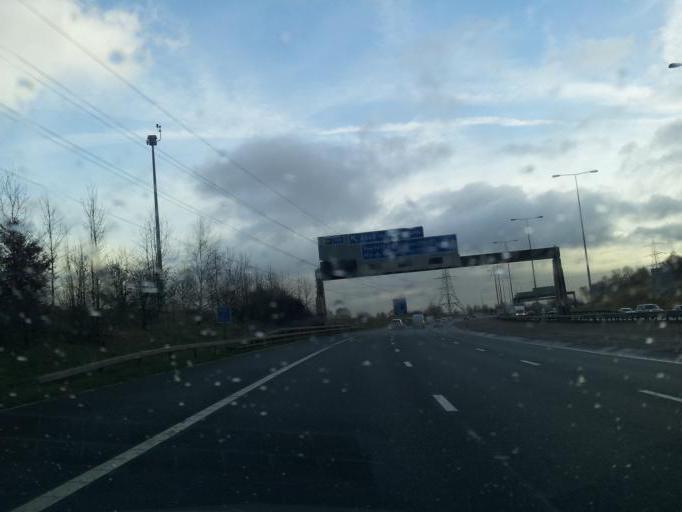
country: GB
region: England
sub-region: Borough of Rochdale
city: Middleton
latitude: 53.5414
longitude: -2.2228
